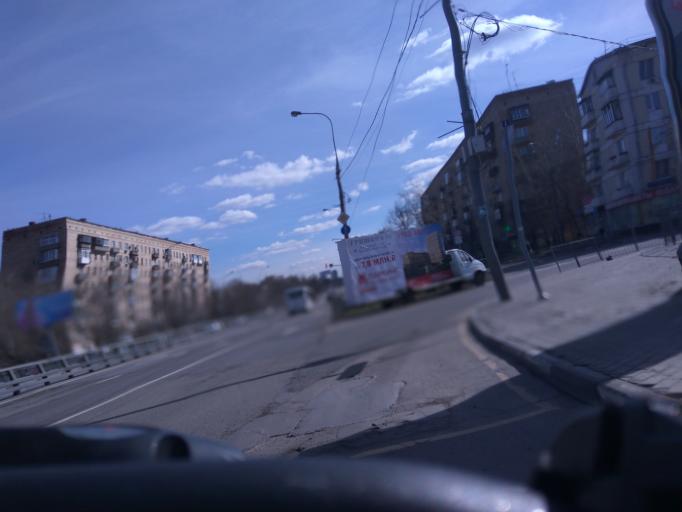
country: RU
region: Moskovskaya
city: Fili
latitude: 55.7388
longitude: 37.4838
